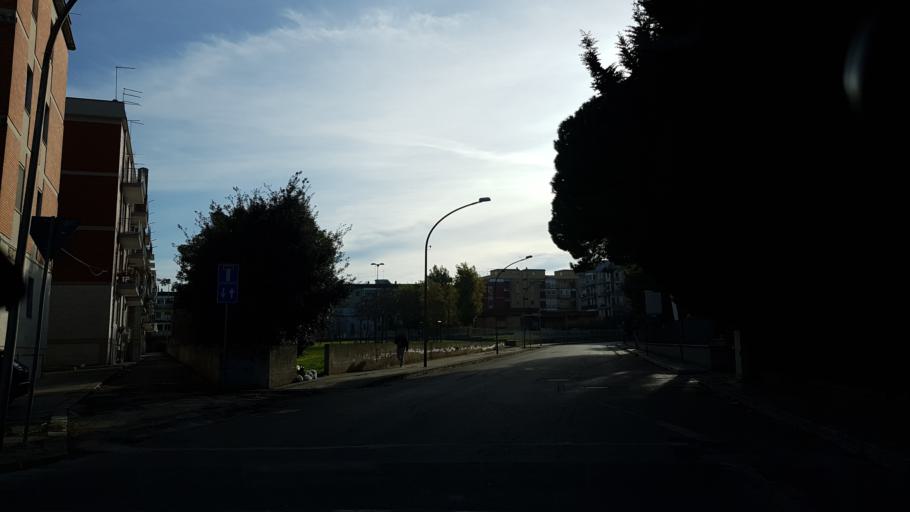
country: IT
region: Apulia
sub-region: Provincia di Brindisi
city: Brindisi
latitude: 40.6213
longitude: 17.9253
